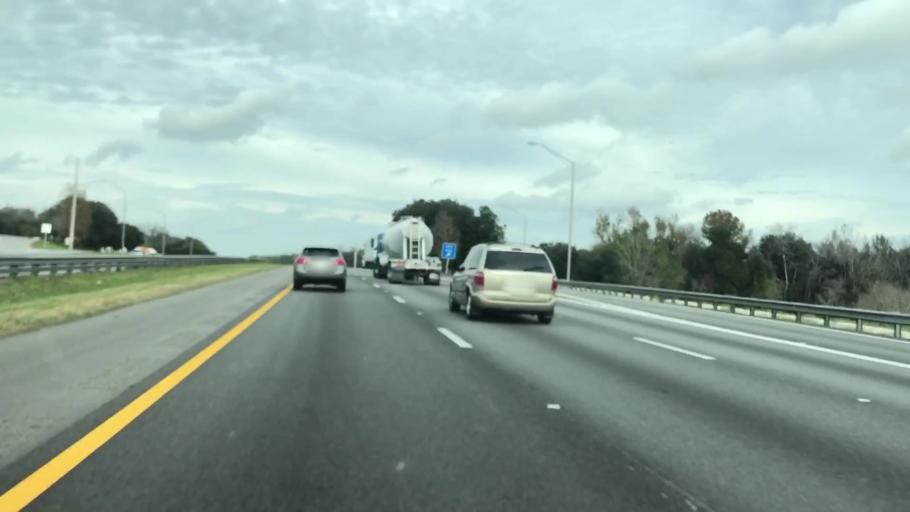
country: US
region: Florida
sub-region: Alachua County
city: Gainesville
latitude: 29.5885
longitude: -82.3613
